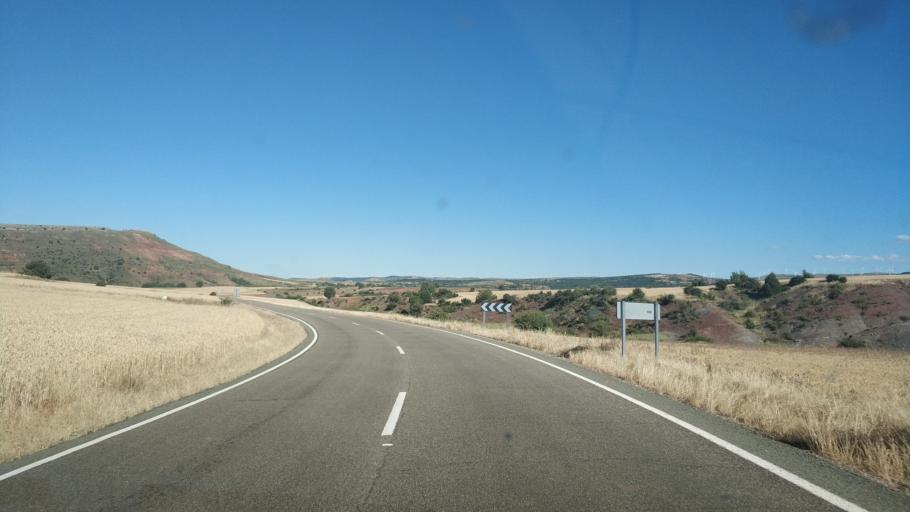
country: ES
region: Castille and Leon
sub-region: Provincia de Soria
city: Montejo de Tiermes
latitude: 41.3481
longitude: -3.1600
